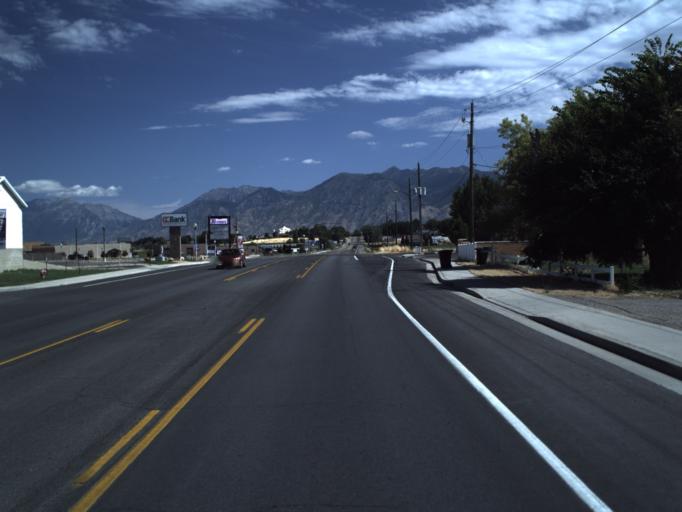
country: US
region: Utah
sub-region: Utah County
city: Salem
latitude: 40.0621
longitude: -111.6679
